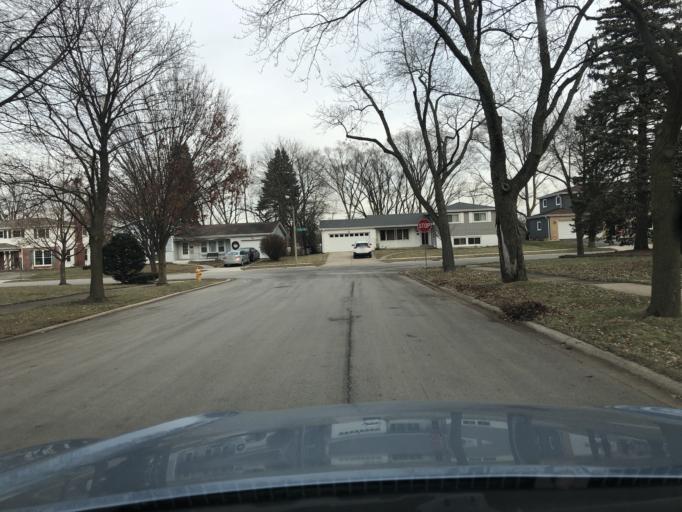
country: US
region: Illinois
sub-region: DuPage County
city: Addison
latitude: 41.9336
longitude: -88.0095
